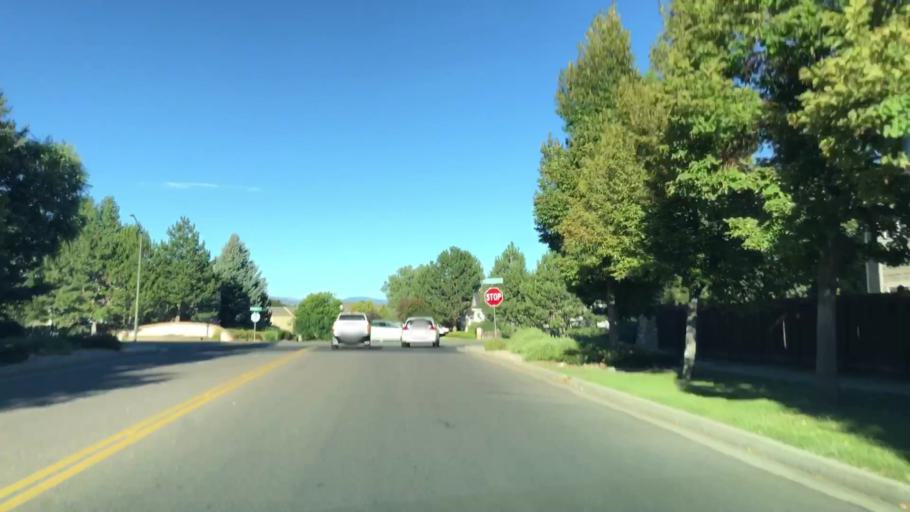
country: US
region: Colorado
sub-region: Larimer County
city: Fort Collins
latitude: 40.5175
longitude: -105.0386
